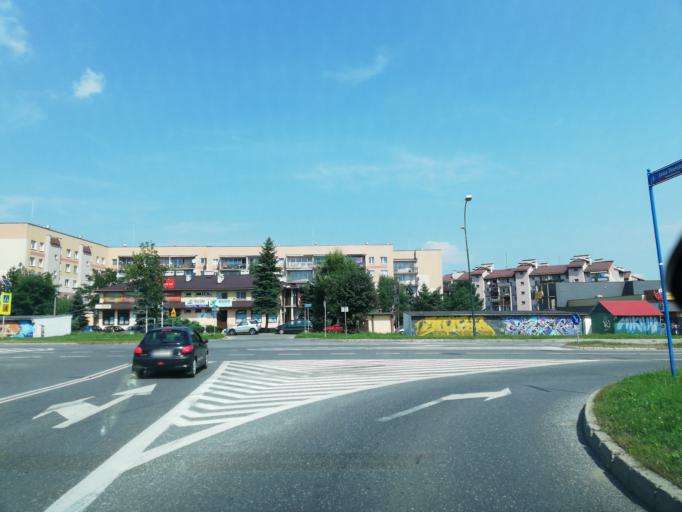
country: PL
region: Lesser Poland Voivodeship
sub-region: Powiat nowosadecki
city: Nowy Sacz
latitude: 49.6085
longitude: 20.7216
